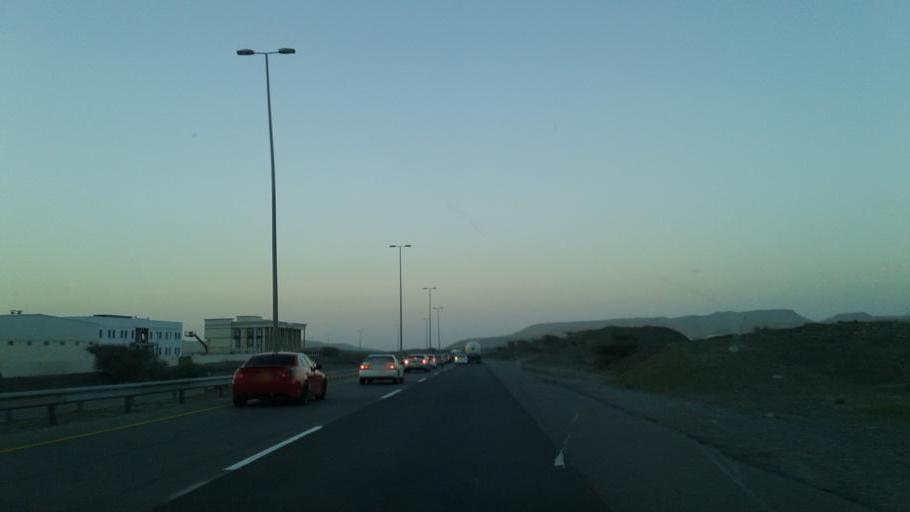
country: OM
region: Muhafazat ad Dakhiliyah
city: Bidbid
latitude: 23.4947
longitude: 58.1963
